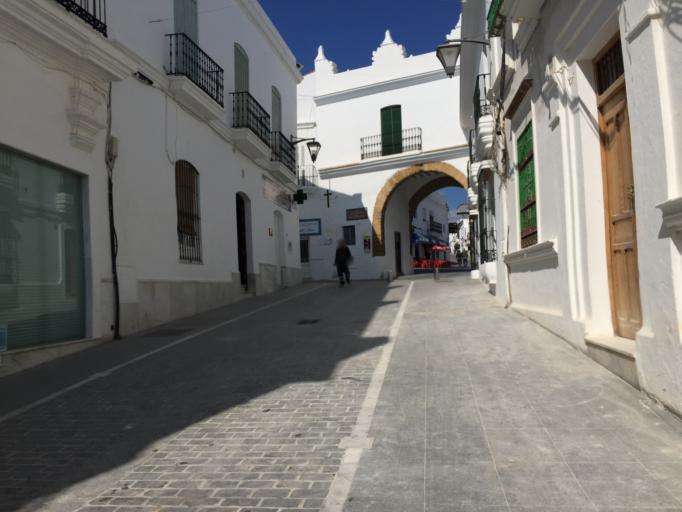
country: ES
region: Andalusia
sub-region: Provincia de Cadiz
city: Conil de la Frontera
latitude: 36.2757
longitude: -6.0879
